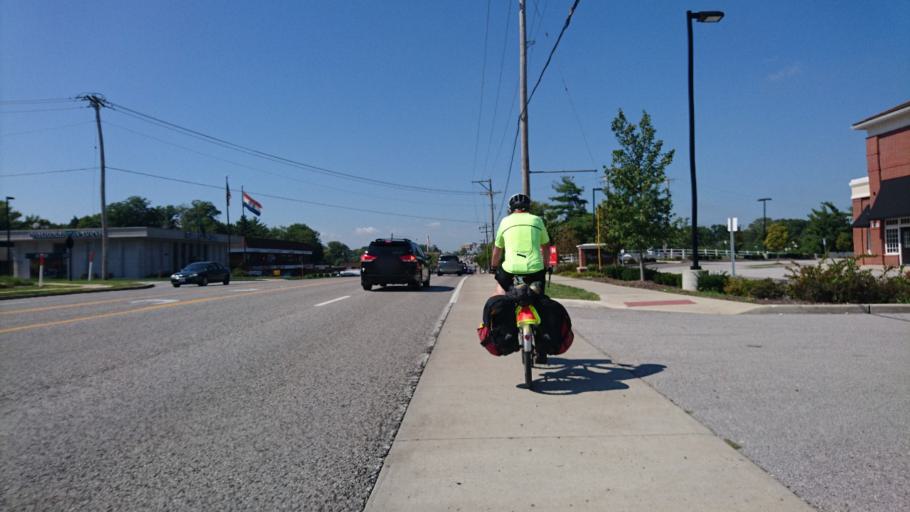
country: US
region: Missouri
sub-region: Saint Louis County
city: Des Peres
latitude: 38.6001
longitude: -90.4271
